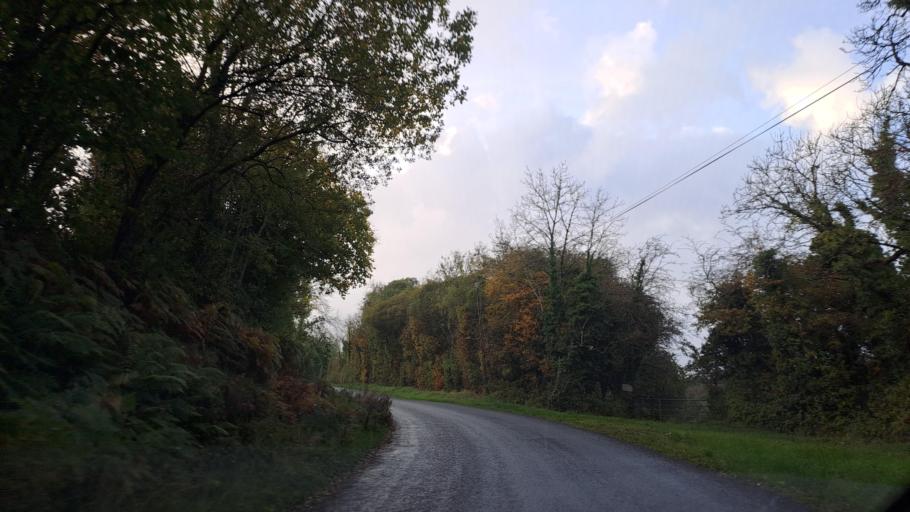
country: IE
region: Ulster
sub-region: County Monaghan
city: Carrickmacross
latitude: 53.9715
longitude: -6.7654
